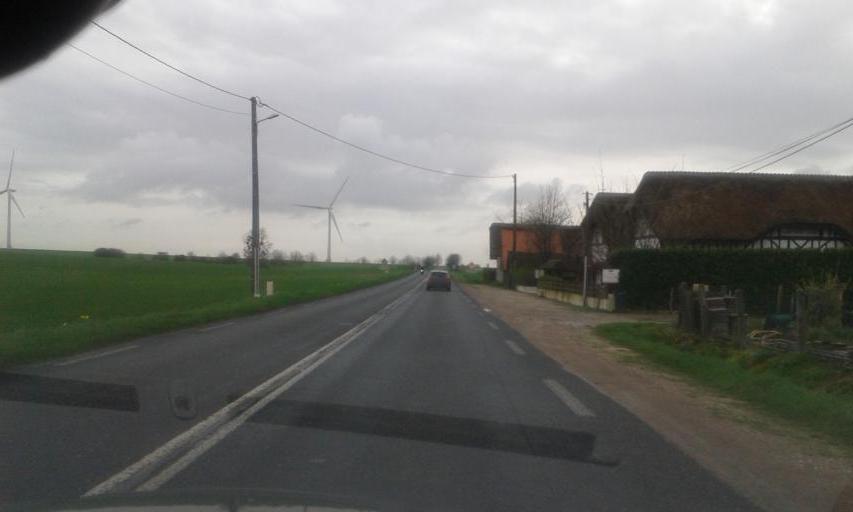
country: FR
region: Haute-Normandie
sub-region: Departement de la Seine-Maritime
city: Montmain
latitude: 49.3872
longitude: 1.2786
